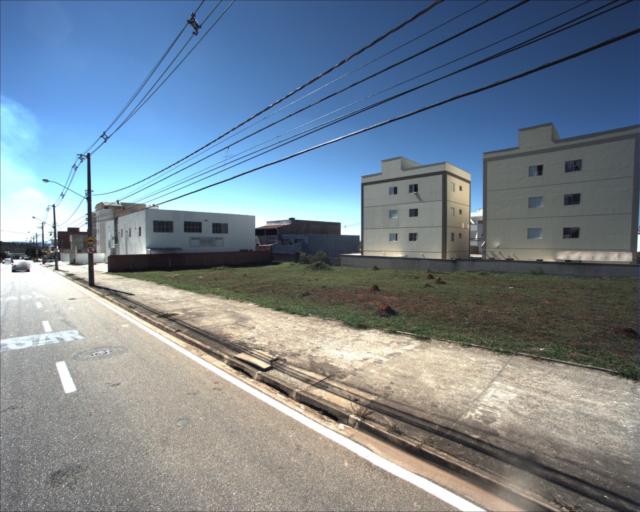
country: BR
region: Sao Paulo
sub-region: Sorocaba
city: Sorocaba
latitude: -23.4802
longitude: -47.5121
